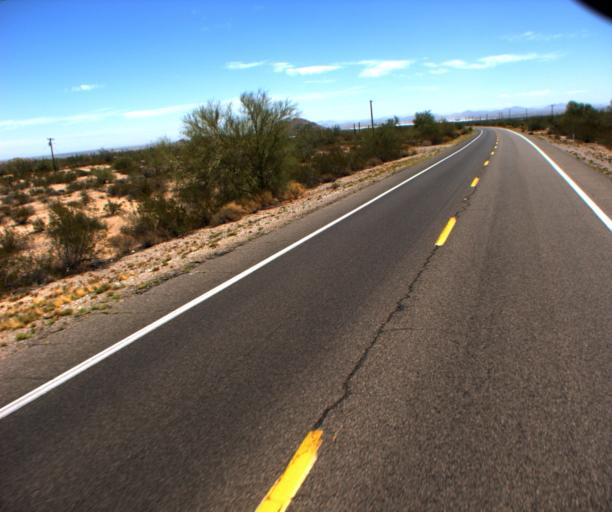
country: US
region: Arizona
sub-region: Pinal County
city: Maricopa
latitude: 32.8445
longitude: -112.0995
